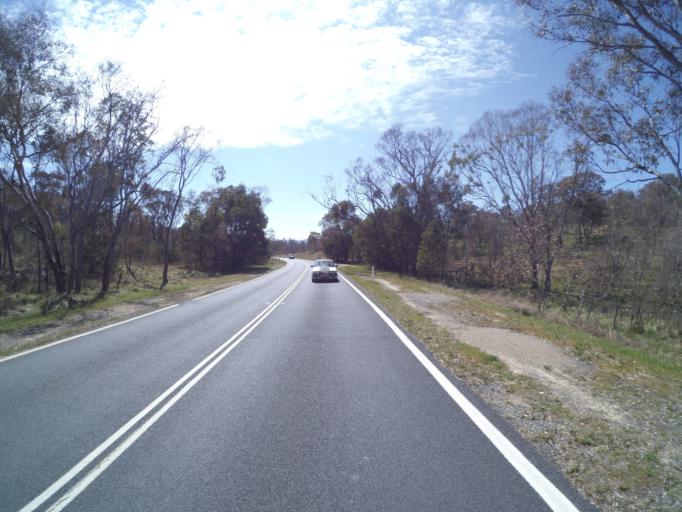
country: AU
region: Australian Capital Territory
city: Macarthur
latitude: -35.4529
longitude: 149.0446
